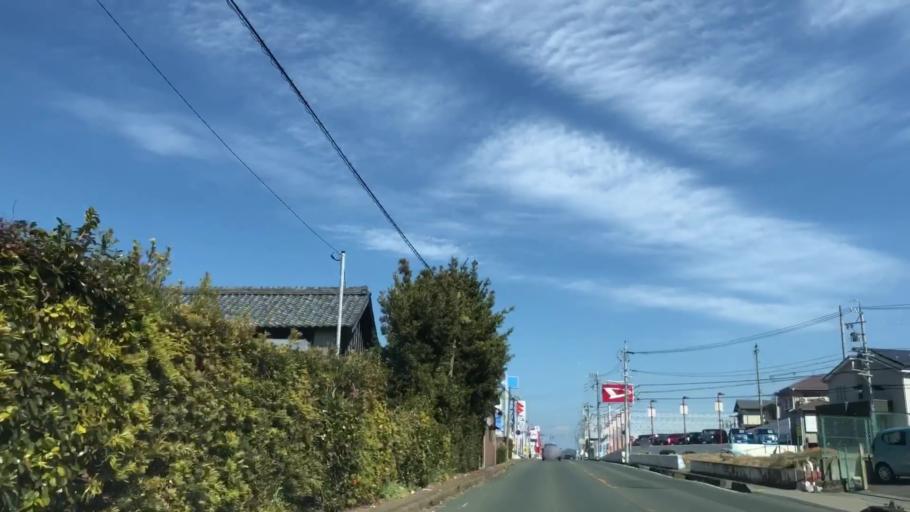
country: JP
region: Aichi
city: Toyohashi
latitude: 34.7231
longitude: 137.3749
